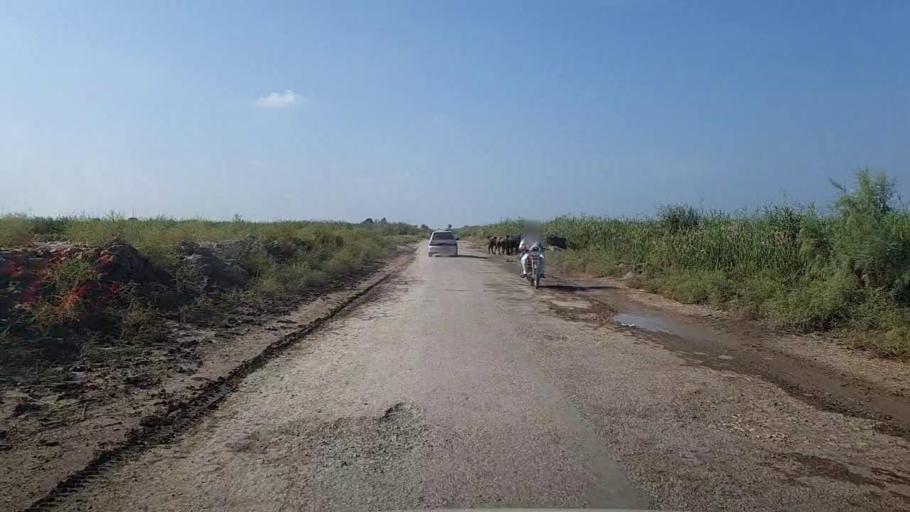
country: PK
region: Sindh
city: Kandiaro
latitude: 27.0666
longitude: 68.3150
